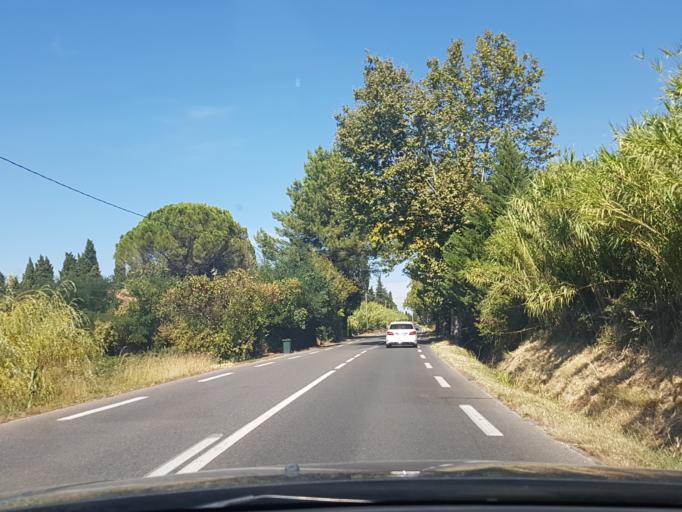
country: FR
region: Provence-Alpes-Cote d'Azur
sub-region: Departement des Bouches-du-Rhone
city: Eyragues
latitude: 43.8251
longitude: 4.8358
